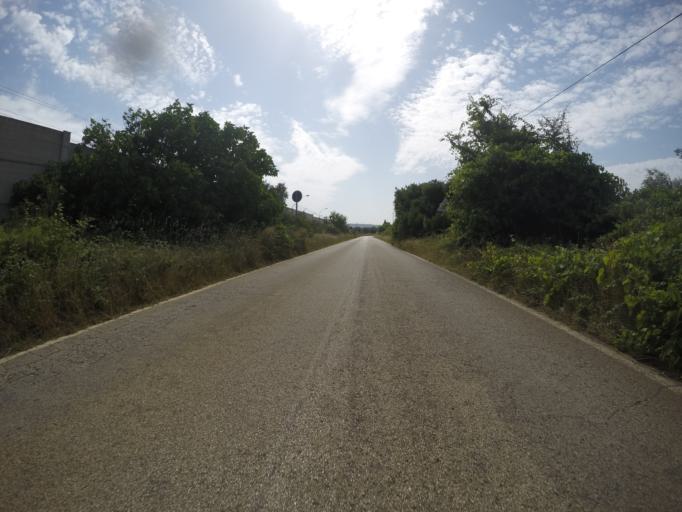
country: IT
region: Apulia
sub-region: Provincia di Taranto
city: Montemesola
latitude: 40.6040
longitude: 17.3745
